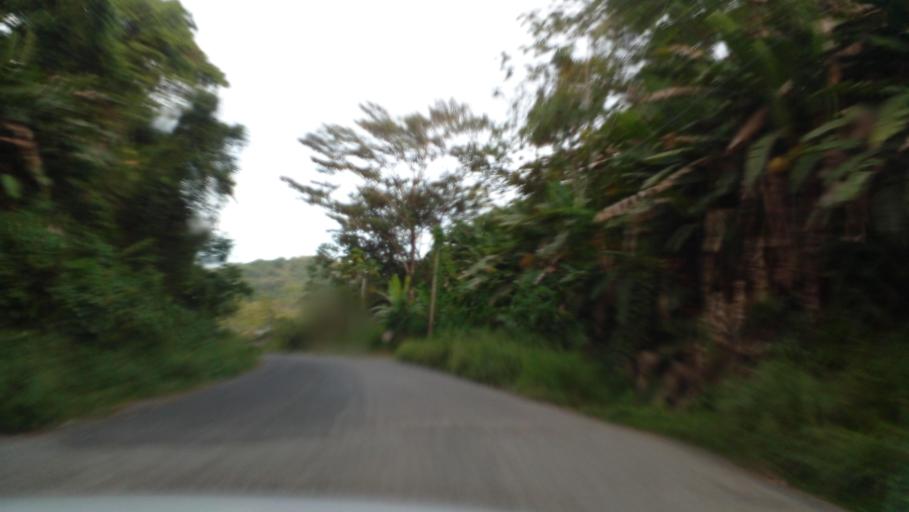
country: PA
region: Bocas del Toro
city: Valle del Risco
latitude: 9.2092
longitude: -82.3699
